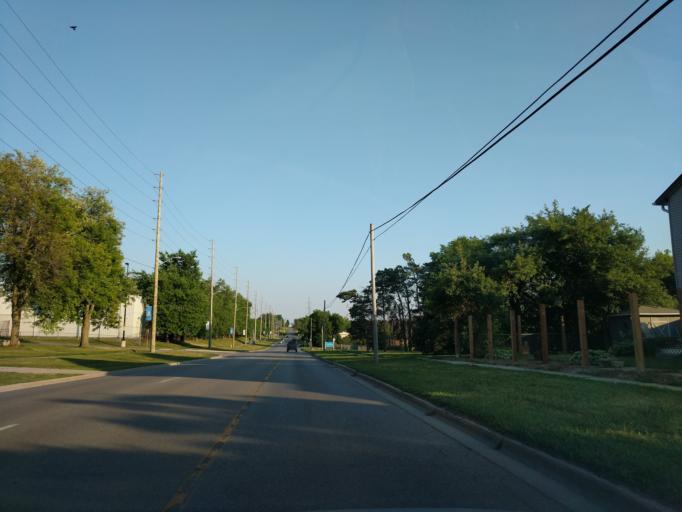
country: CA
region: Ontario
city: Oshawa
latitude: 43.8873
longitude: -78.8915
